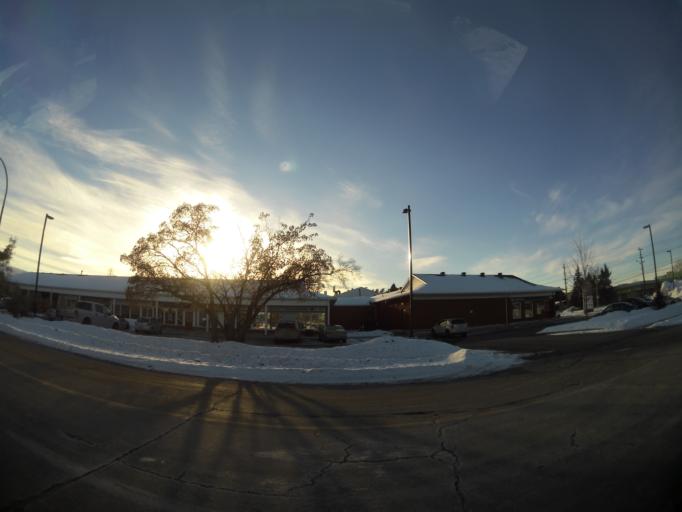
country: CA
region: Ontario
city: Ottawa
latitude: 45.4311
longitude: -75.5642
